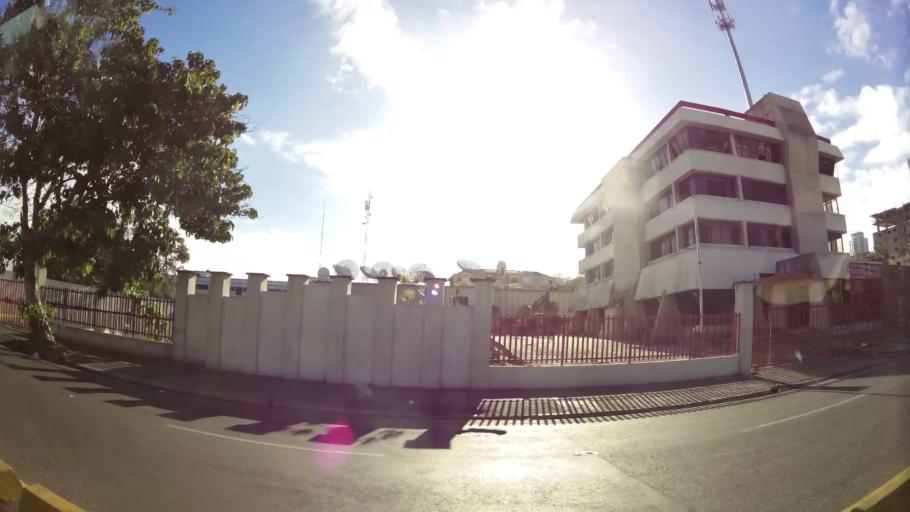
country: DO
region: Nacional
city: La Julia
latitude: 18.4815
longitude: -69.9311
